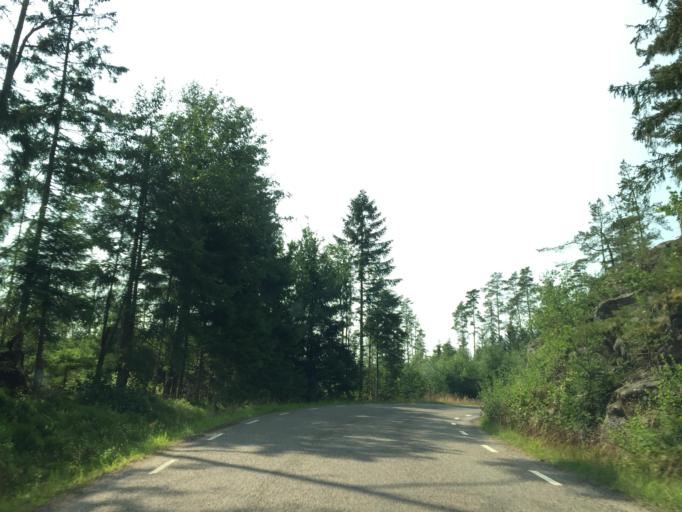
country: SE
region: Vaestra Goetaland
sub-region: Trollhattan
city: Sjuntorp
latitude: 58.3096
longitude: 12.1240
